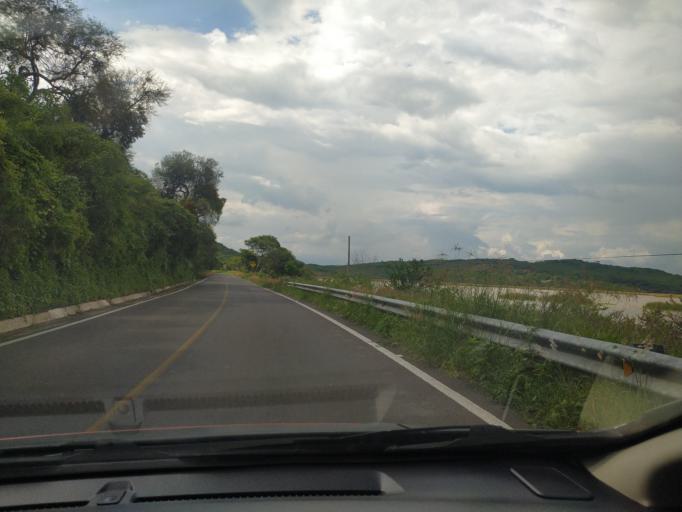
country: MX
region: Jalisco
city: Villa Corona
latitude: 20.3596
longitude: -103.6669
